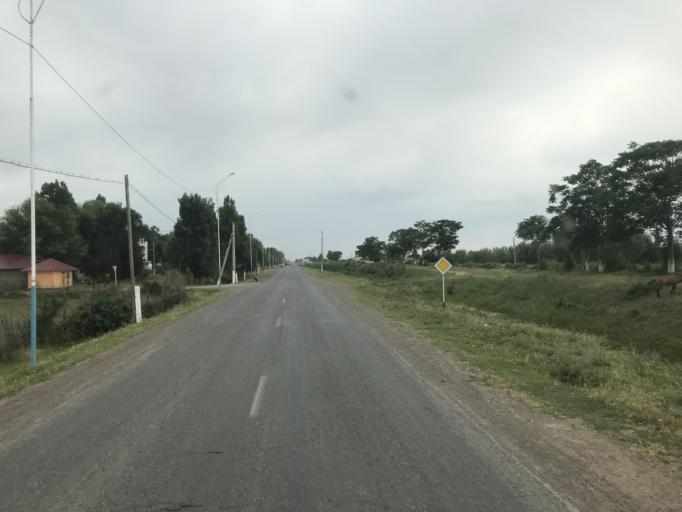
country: KZ
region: Ongtustik Qazaqstan
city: Asykata
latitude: 40.9384
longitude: 68.4125
